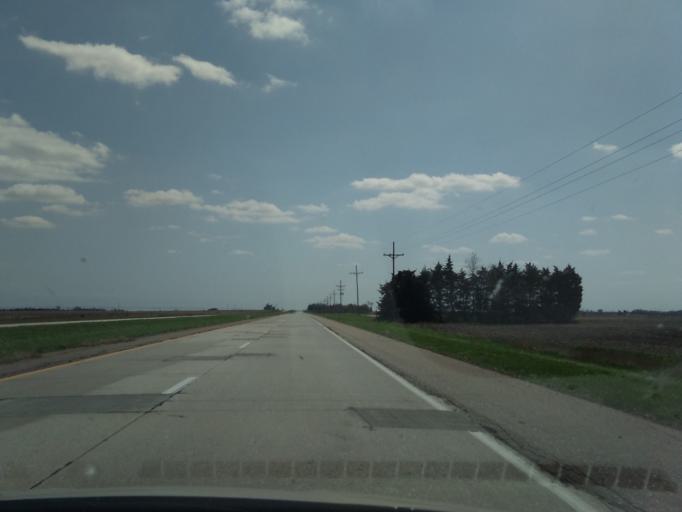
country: US
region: Nebraska
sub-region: Thayer County
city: Hebron
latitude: 40.3030
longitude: -97.5768
